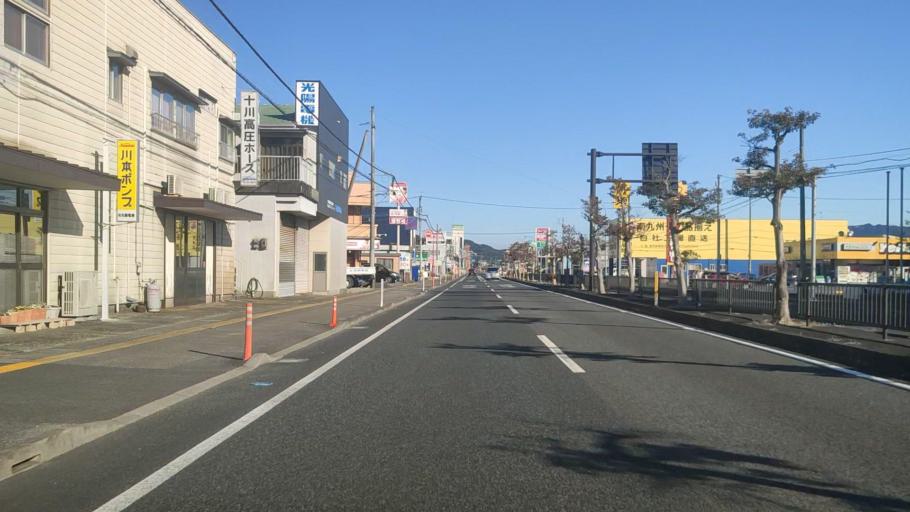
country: JP
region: Miyazaki
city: Nobeoka
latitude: 32.5914
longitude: 131.6761
